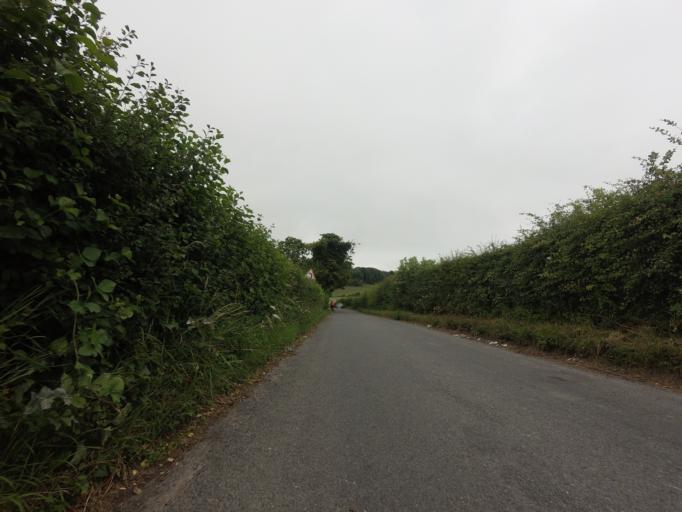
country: GB
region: England
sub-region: Kent
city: Borough Green
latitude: 51.3114
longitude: 0.2697
